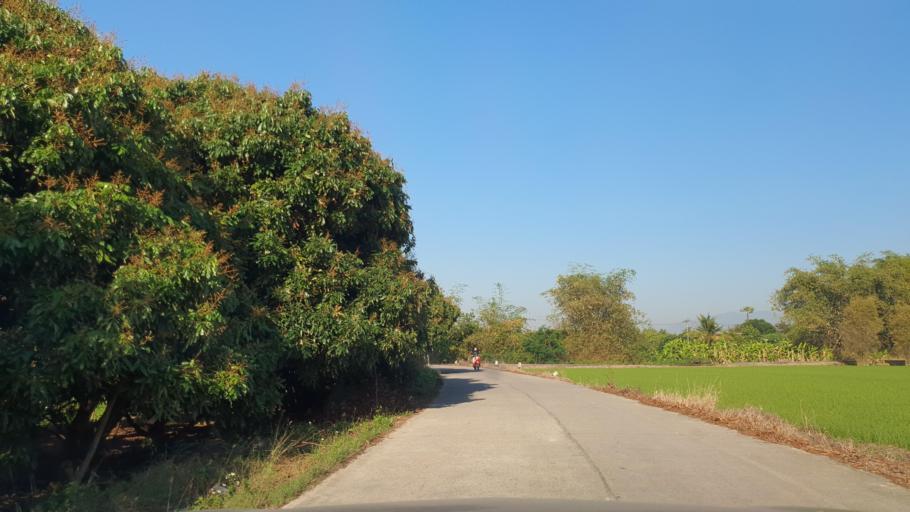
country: TH
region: Chiang Mai
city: Saraphi
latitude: 18.6820
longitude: 99.0772
